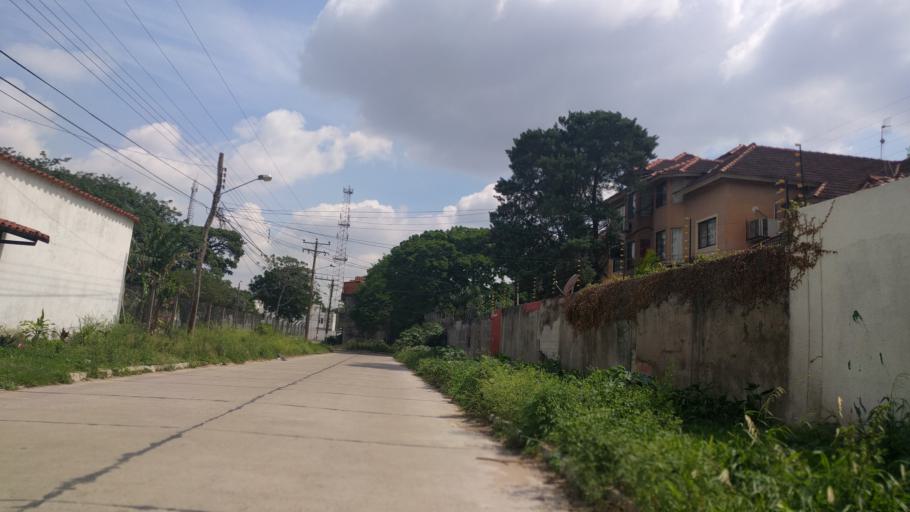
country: BO
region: Santa Cruz
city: Santa Cruz de la Sierra
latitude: -17.7905
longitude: -63.2226
